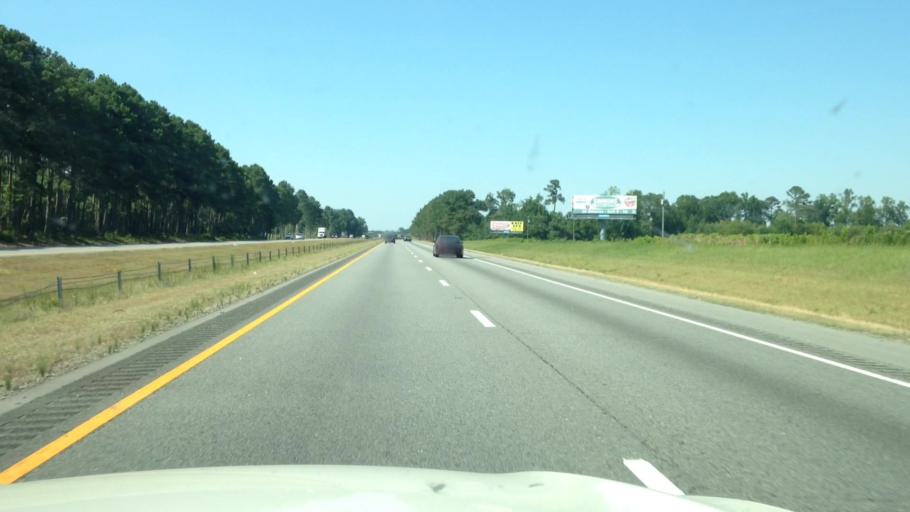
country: US
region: North Carolina
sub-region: Halifax County
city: Enfield
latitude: 36.1998
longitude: -77.7586
